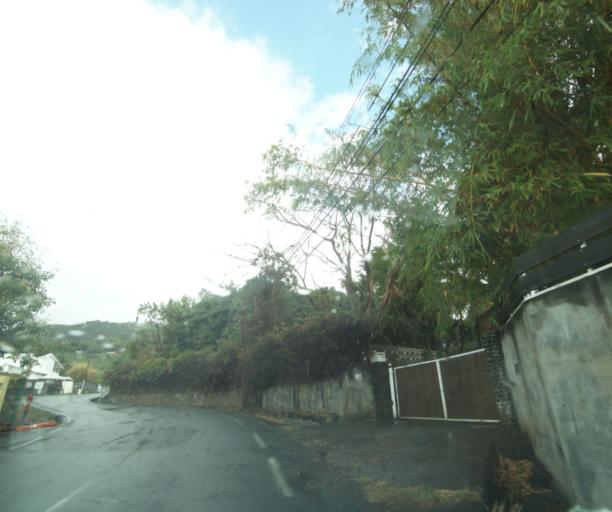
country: RE
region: Reunion
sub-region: Reunion
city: La Possession
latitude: -20.9823
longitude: 55.3331
